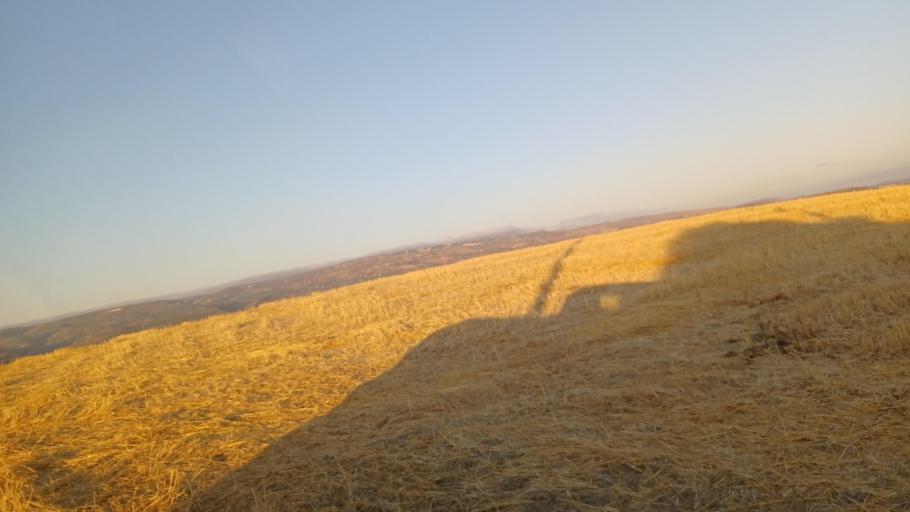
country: CY
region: Pafos
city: Polis
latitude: 34.9938
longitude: 32.4718
